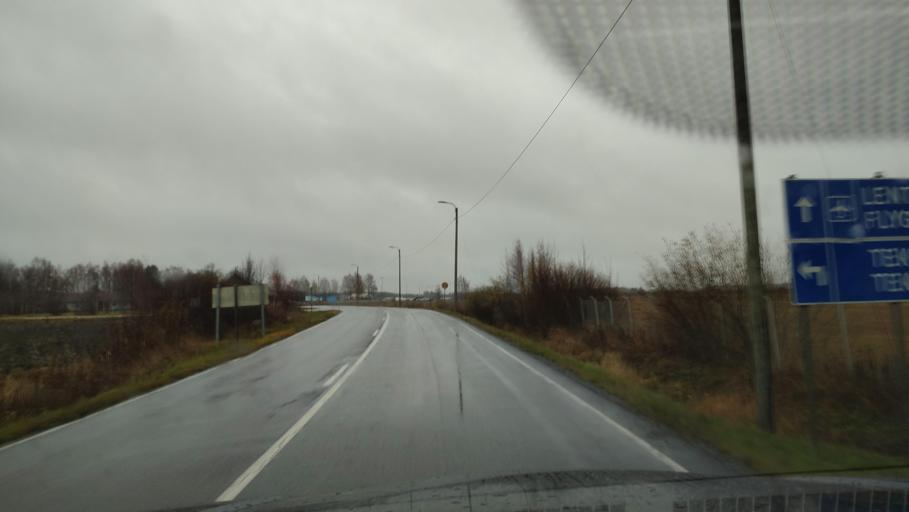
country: FI
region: Ostrobothnia
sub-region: Vaasa
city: Ristinummi
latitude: 63.0442
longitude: 21.7508
